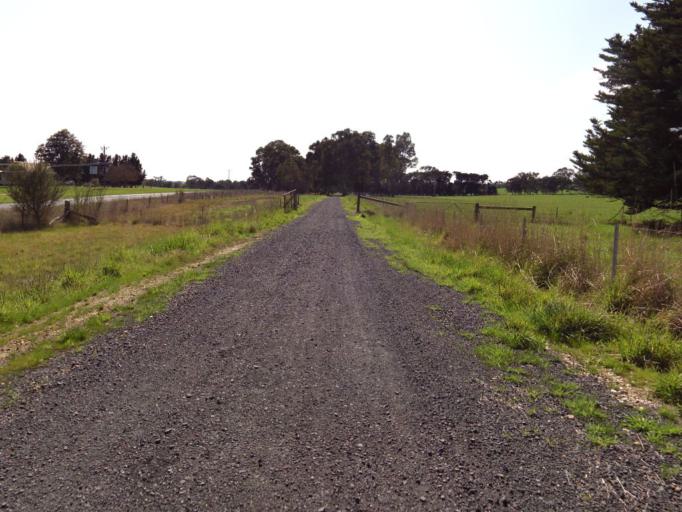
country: AU
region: Victoria
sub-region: Murrindindi
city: Alexandra
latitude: -37.1272
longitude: 145.5972
